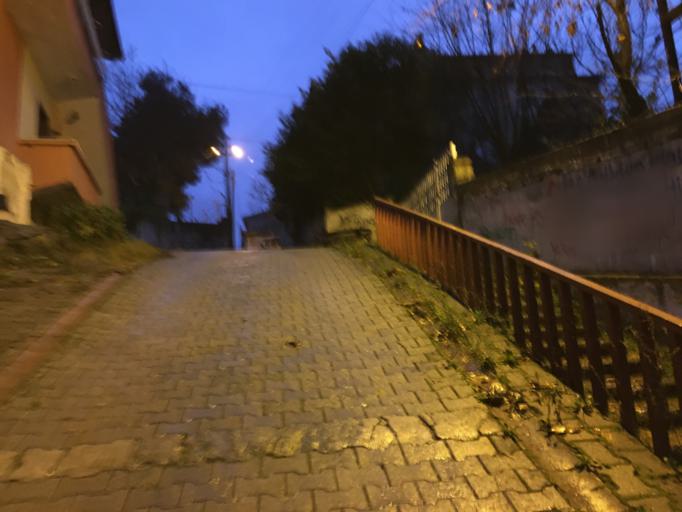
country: TR
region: Samsun
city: Alacam
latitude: 41.6122
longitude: 35.6062
